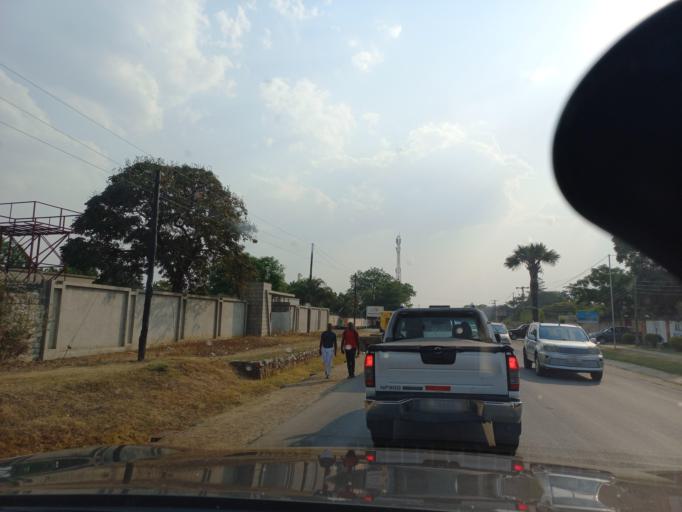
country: ZM
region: Lusaka
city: Lusaka
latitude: -15.4604
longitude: 28.2519
